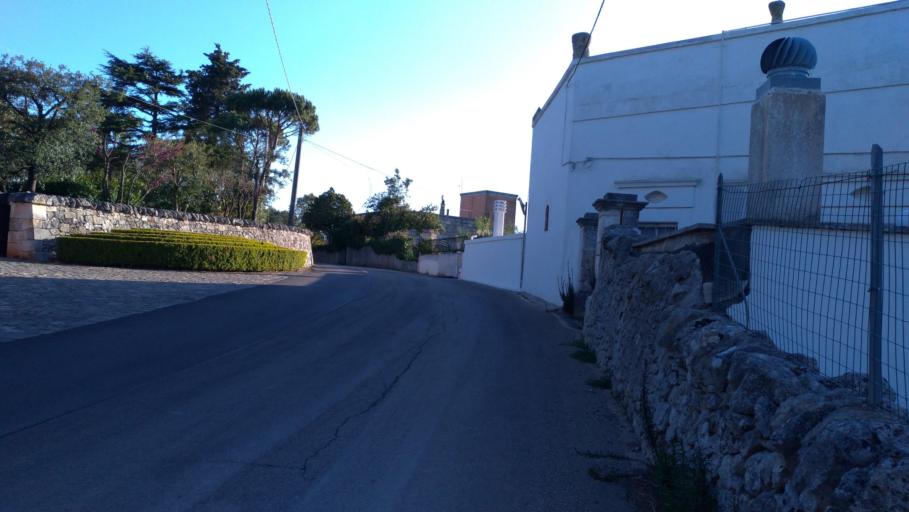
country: IT
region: Apulia
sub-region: Provincia di Taranto
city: Martina Franca
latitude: 40.6910
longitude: 17.3370
